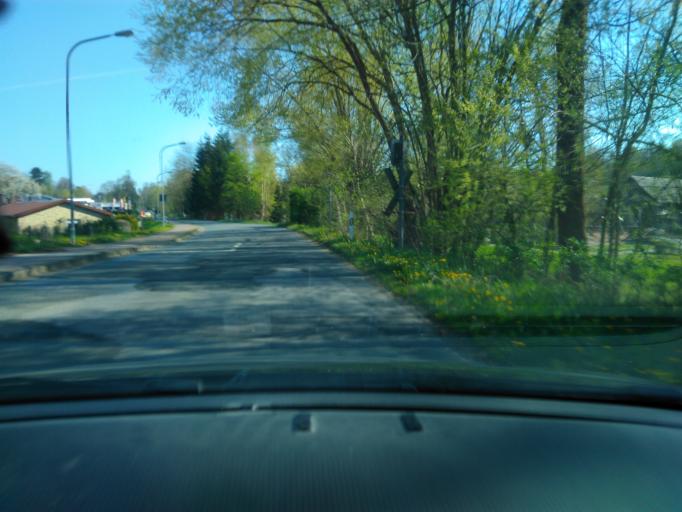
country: DE
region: Lower Saxony
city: Osterode am Harz
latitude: 51.7173
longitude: 10.2723
